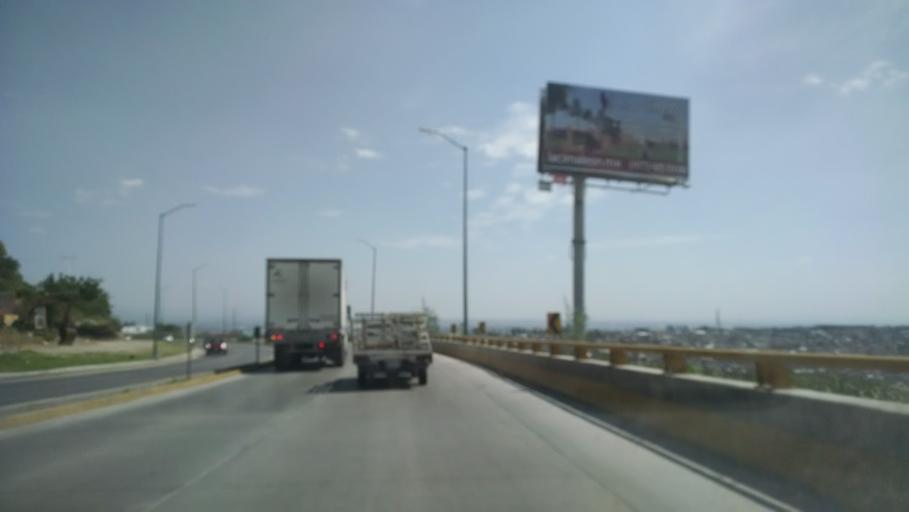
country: MX
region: Guanajuato
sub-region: Leon
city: La Ermita
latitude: 21.1464
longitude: -101.7165
